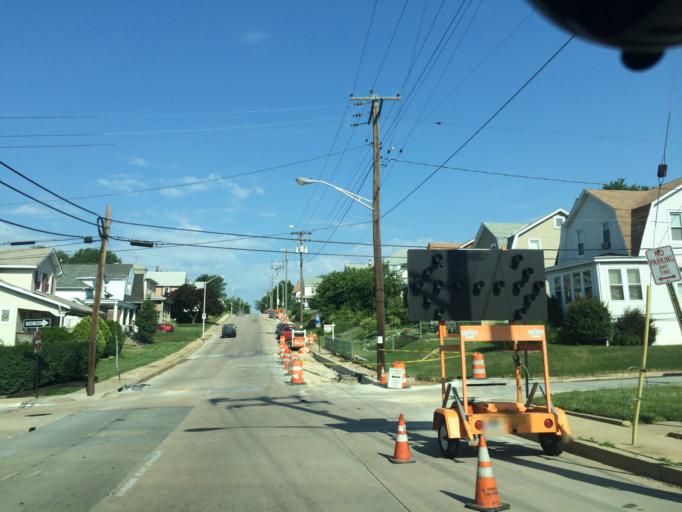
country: US
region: Maryland
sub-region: Baltimore County
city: Overlea
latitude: 39.3564
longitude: -76.5292
